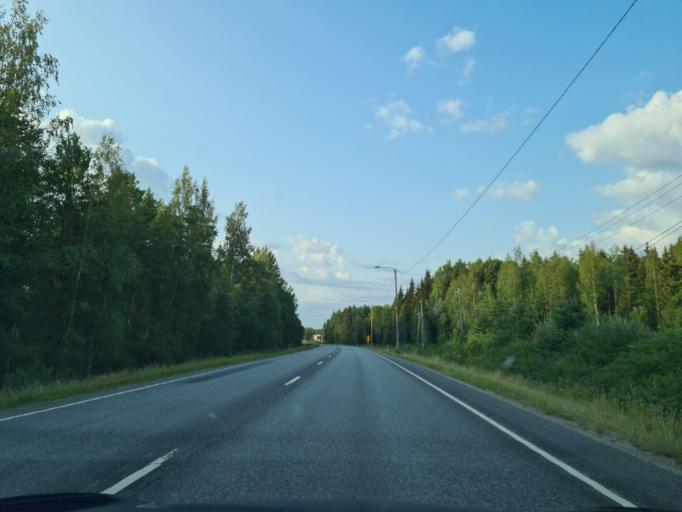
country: FI
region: Southern Ostrobothnia
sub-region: Seinaejoki
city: Kauhava
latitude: 63.0754
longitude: 23.0560
